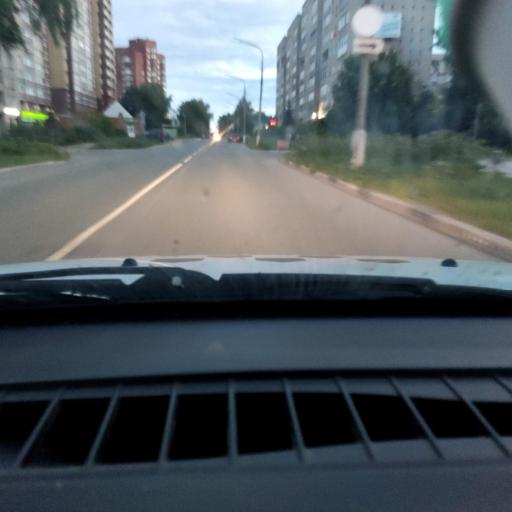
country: RU
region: Udmurtiya
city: Glazov
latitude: 58.1368
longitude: 52.6782
